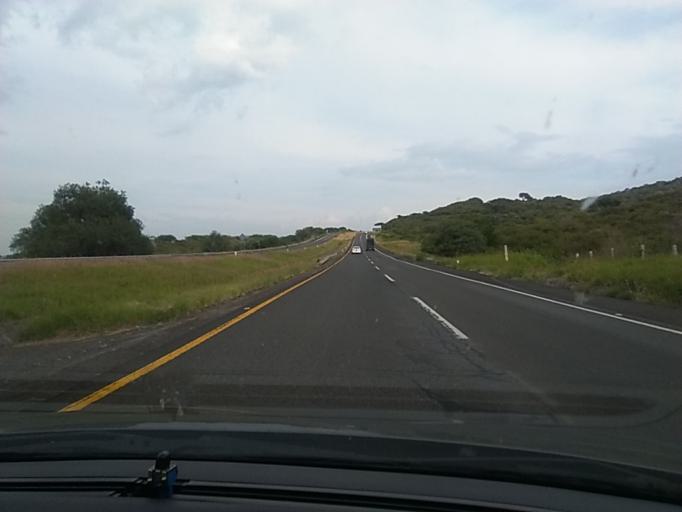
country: MX
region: Michoacan
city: Copandaro de Galeana
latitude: 19.8913
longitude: -101.2390
